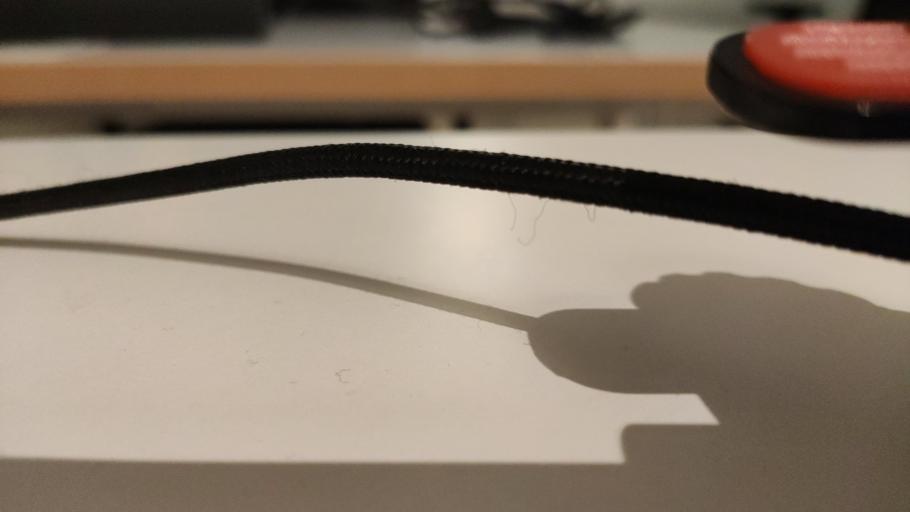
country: RU
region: Moskovskaya
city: Dmitrov
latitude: 56.3539
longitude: 37.5091
